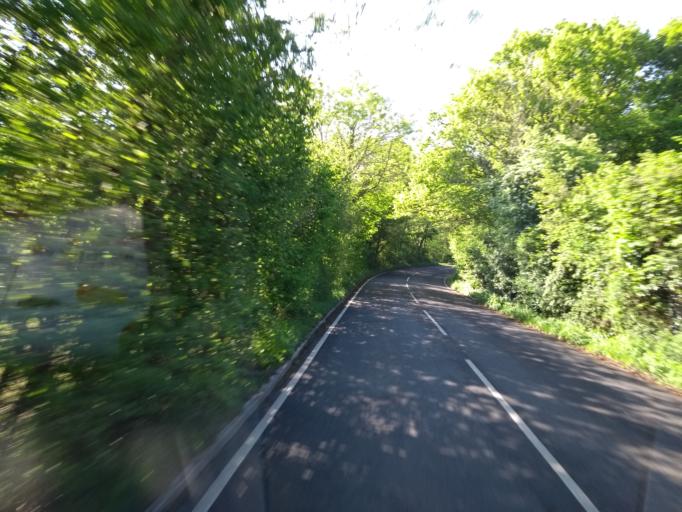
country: GB
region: England
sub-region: Somerset
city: Taunton
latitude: 50.9560
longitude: -3.0815
